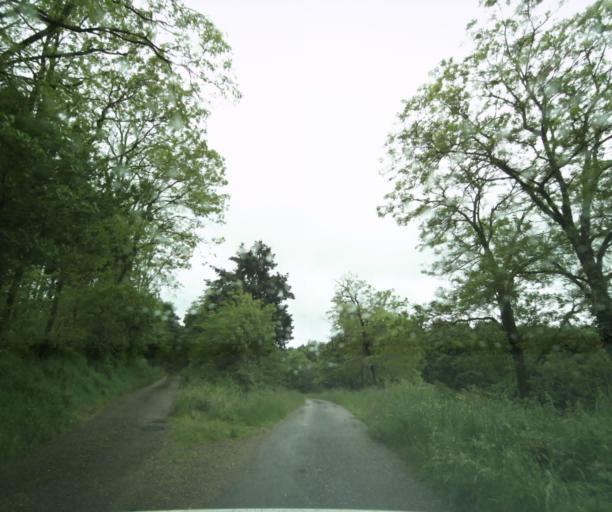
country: FR
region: Bourgogne
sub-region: Departement de Saone-et-Loire
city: Matour
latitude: 46.4527
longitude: 4.4648
